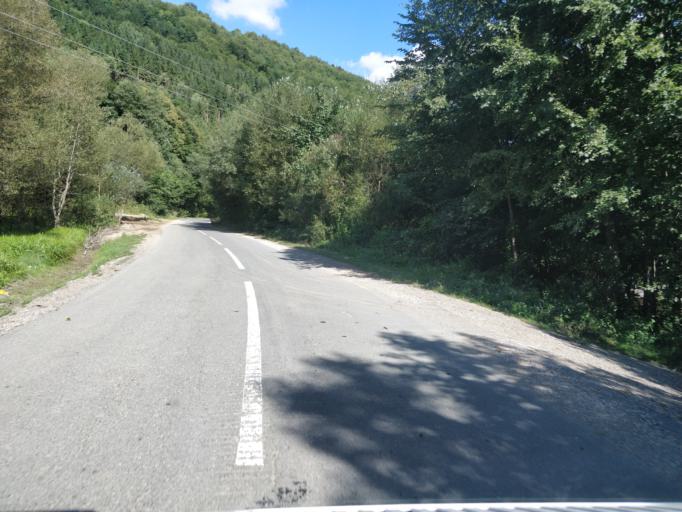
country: RO
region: Cluj
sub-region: Comuna Sacueu
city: Sacuieu
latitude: 46.8499
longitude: 22.8627
